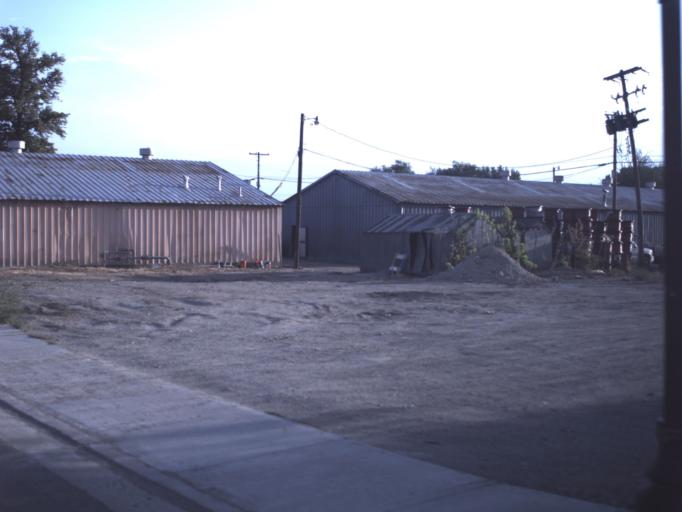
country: US
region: Utah
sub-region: Salt Lake County
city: Midvale
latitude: 40.6140
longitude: -111.8908
